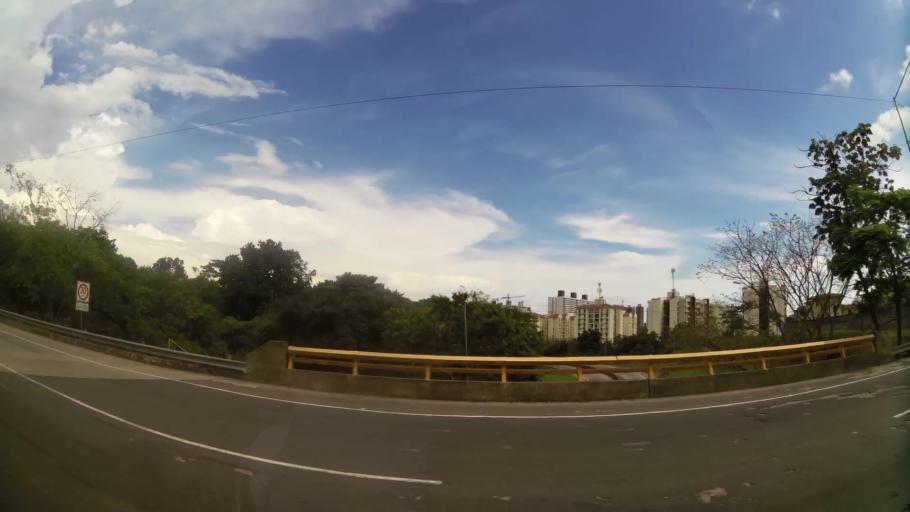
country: PA
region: Panama
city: Panama
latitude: 9.0393
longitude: -79.5326
